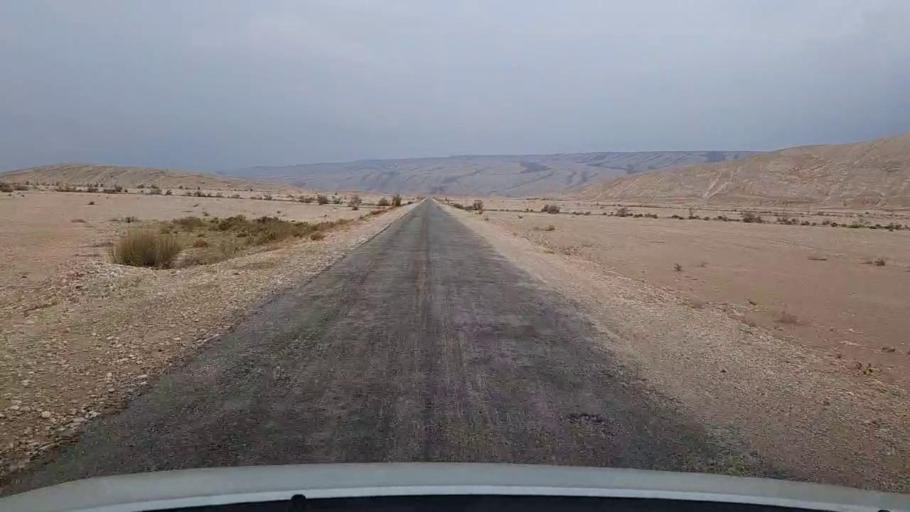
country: PK
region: Sindh
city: Sehwan
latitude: 26.2384
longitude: 67.7120
